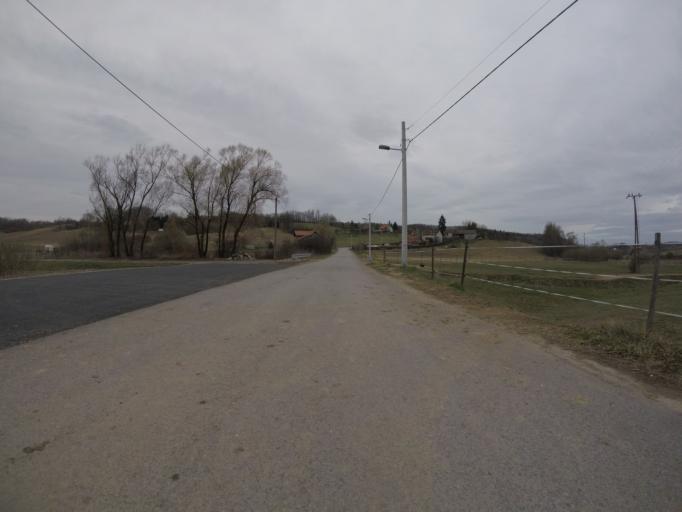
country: HR
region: Grad Zagreb
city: Strmec
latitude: 45.6232
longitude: 15.9336
